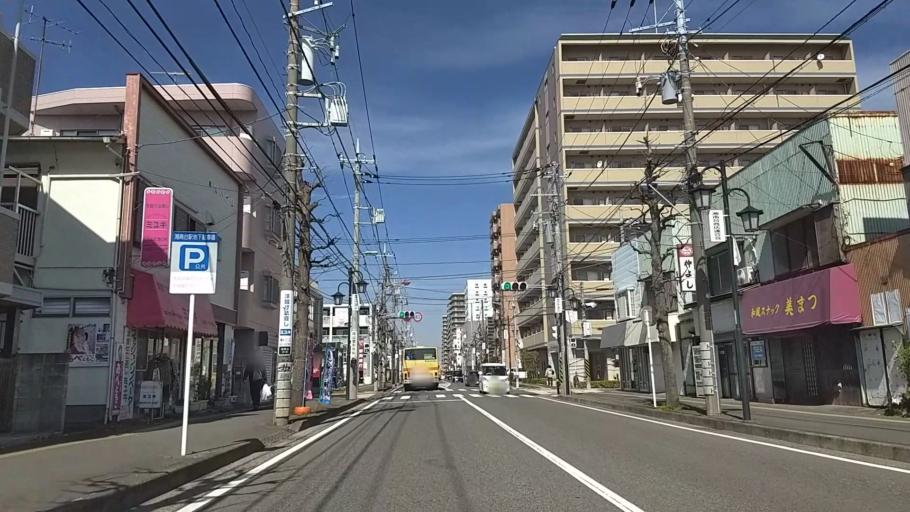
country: JP
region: Kanagawa
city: Fujisawa
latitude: 35.3942
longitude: 139.4635
